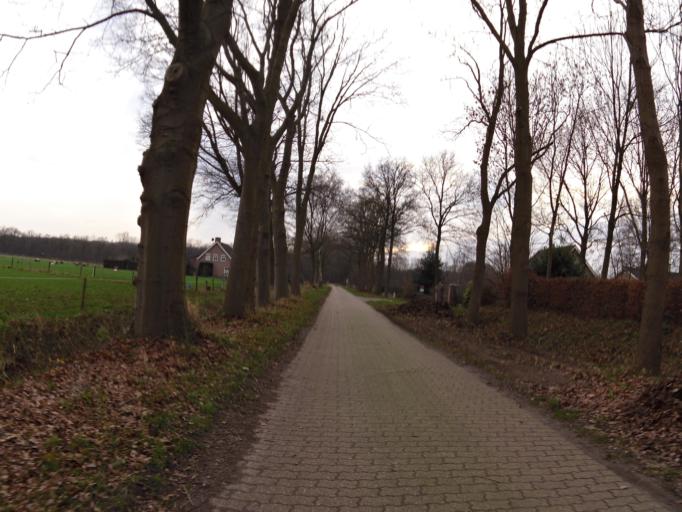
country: NL
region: North Brabant
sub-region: Gemeente Sint-Michielsgestel
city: Sint-Michielsgestel
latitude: 51.6349
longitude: 5.3249
